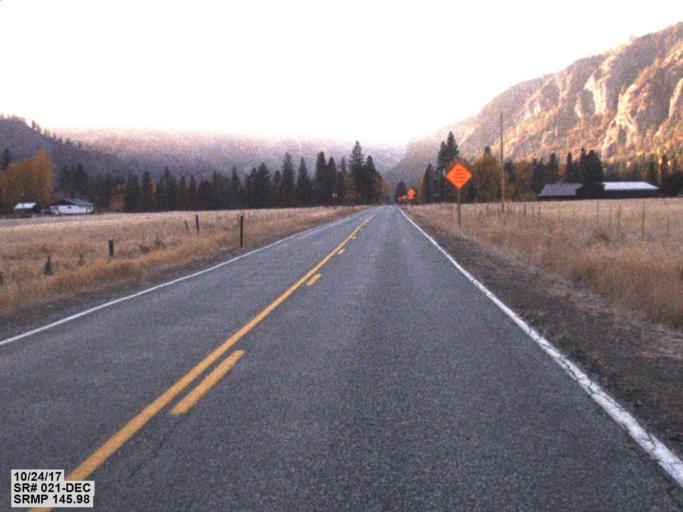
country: US
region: Washington
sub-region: Ferry County
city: Republic
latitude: 48.4638
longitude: -118.7531
